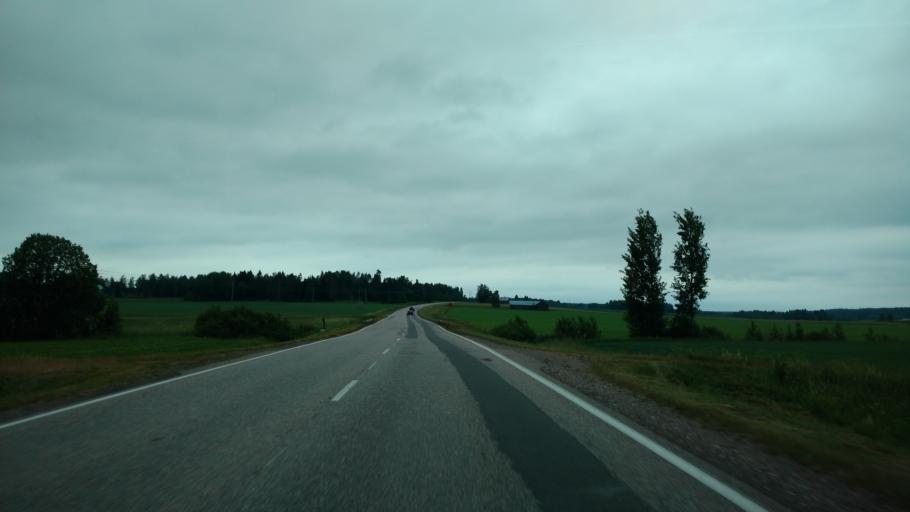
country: FI
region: Varsinais-Suomi
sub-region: Salo
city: Kiikala
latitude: 60.3957
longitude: 23.5846
